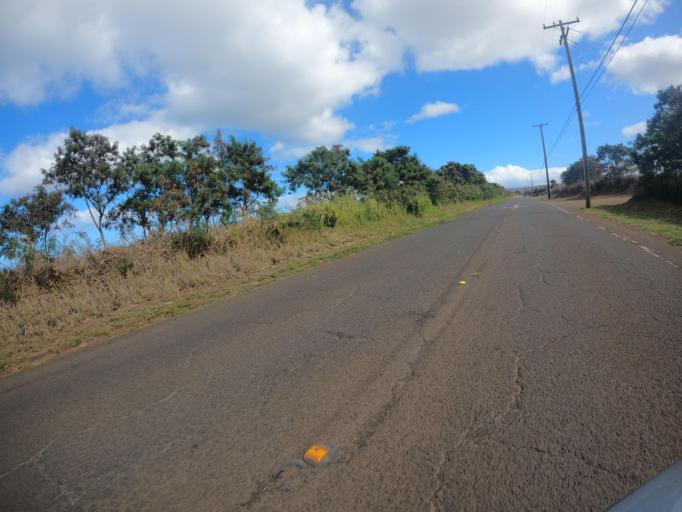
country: US
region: Hawaii
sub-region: Honolulu County
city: Mokuleia
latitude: 21.5721
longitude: -158.1462
